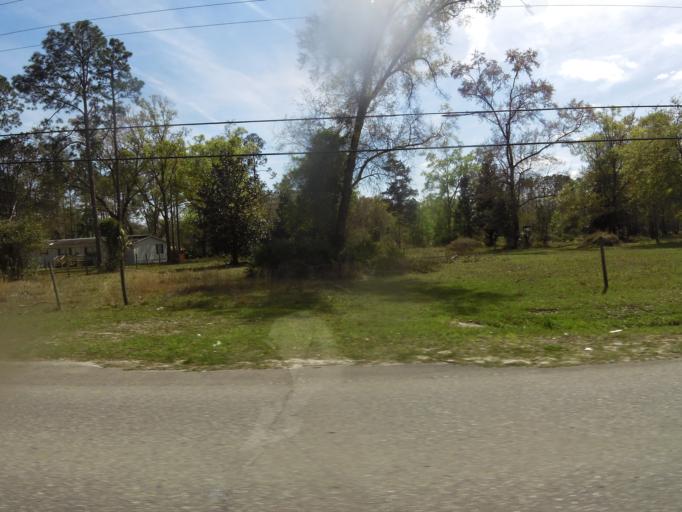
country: US
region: Florida
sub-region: Clay County
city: Middleburg
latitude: 30.1140
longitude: -81.8663
